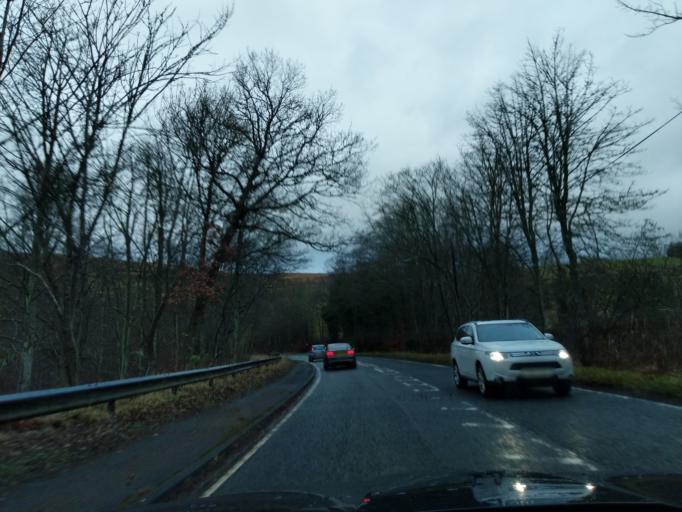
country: GB
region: Scotland
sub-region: The Scottish Borders
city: Galashiels
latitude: 55.6359
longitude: -2.8271
